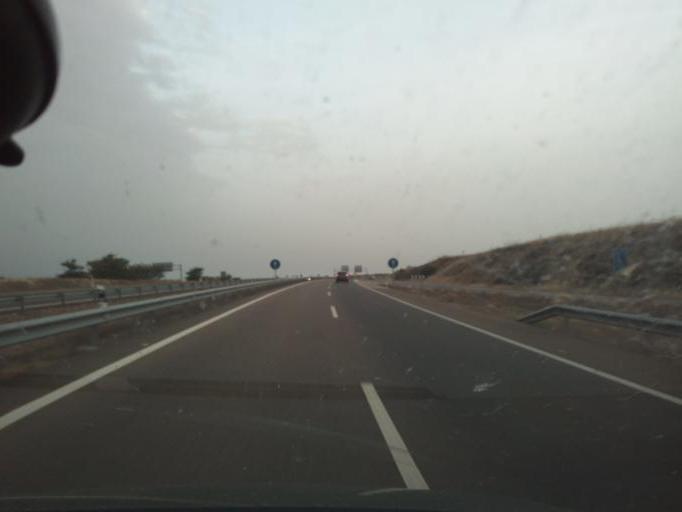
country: ES
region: Extremadura
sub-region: Provincia de Badajoz
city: Merida
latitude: 38.9434
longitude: -6.3436
